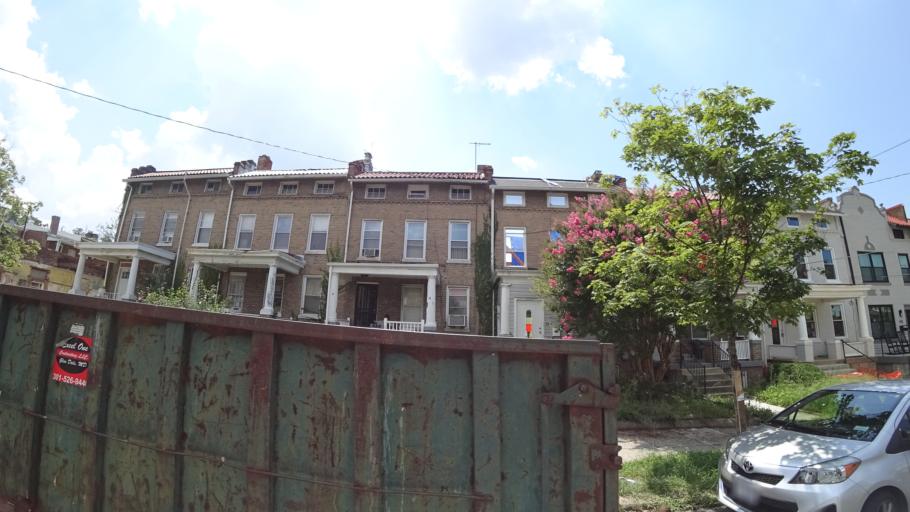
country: US
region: Maryland
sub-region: Prince George's County
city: Chillum
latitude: 38.9389
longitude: -77.0178
